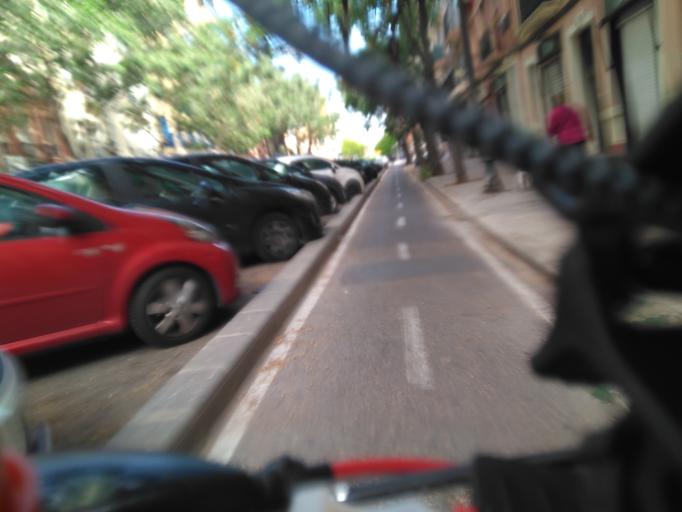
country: ES
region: Valencia
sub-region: Provincia de Valencia
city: Valencia
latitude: 39.4714
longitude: -0.3898
